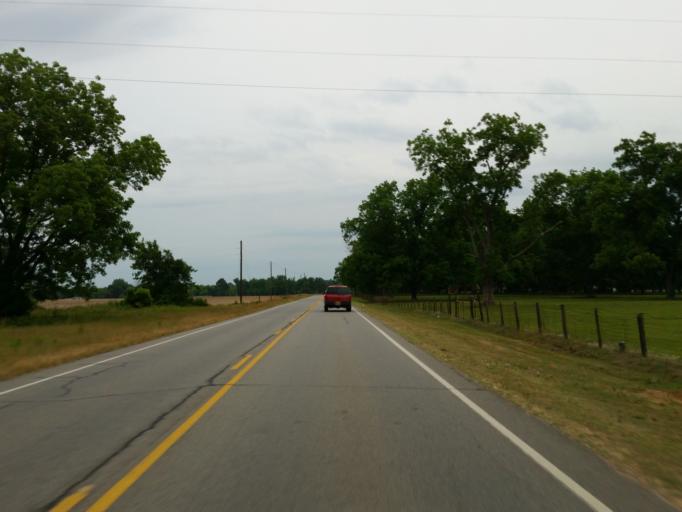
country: US
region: Georgia
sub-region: Dooly County
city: Vienna
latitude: 32.1153
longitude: -83.7981
